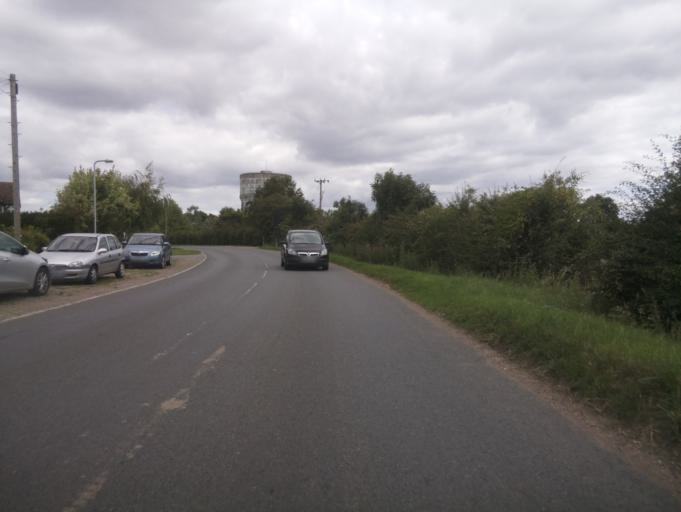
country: GB
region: England
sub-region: Buckinghamshire
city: Newton Longville
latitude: 51.9537
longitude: -0.8137
